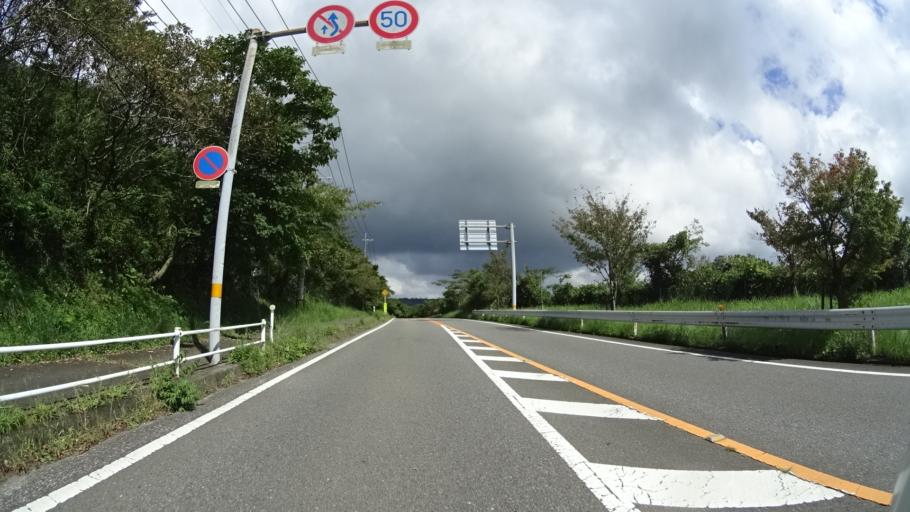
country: JP
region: Oita
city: Hiji
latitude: 33.3462
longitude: 131.4562
